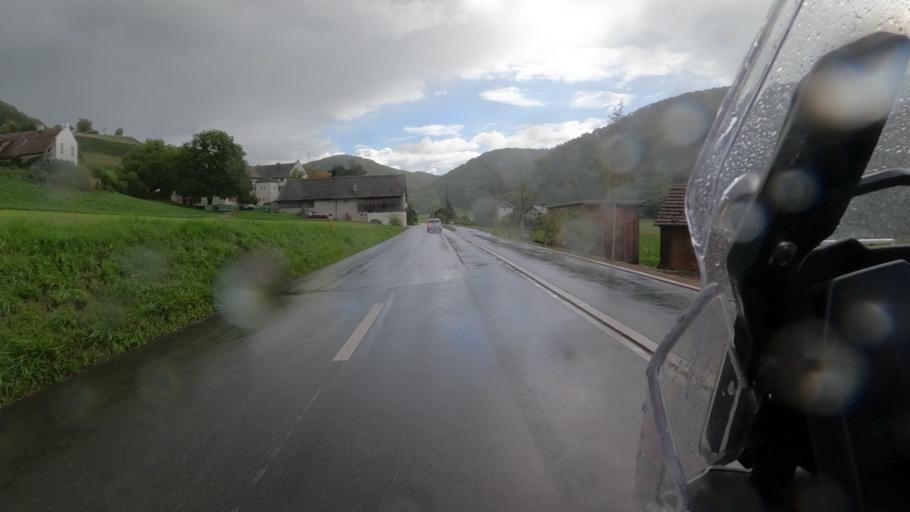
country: CH
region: Schaffhausen
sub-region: Bezirk Unterklettgau
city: Wilchingen
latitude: 47.6576
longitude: 8.4828
